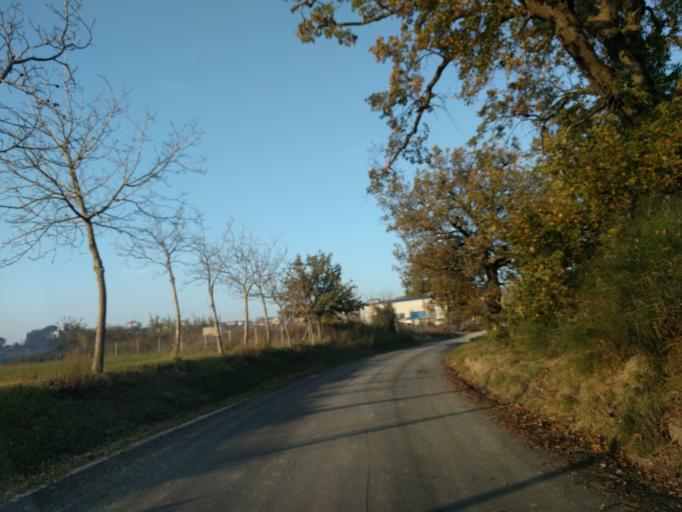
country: IT
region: The Marches
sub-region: Provincia di Pesaro e Urbino
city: Orciano di Pesaro
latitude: 43.6832
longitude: 12.9760
